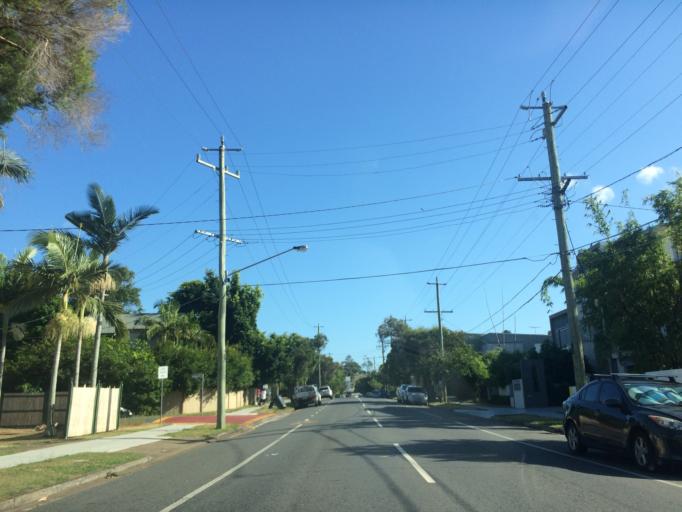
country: AU
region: Queensland
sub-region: Brisbane
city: Balmoral
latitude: -27.4558
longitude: 153.0615
